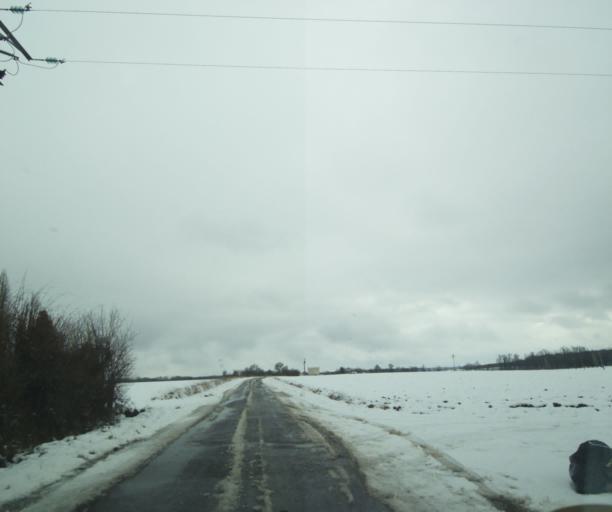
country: FR
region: Champagne-Ardenne
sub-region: Departement de la Haute-Marne
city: Montier-en-Der
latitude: 48.4190
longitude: 4.7318
